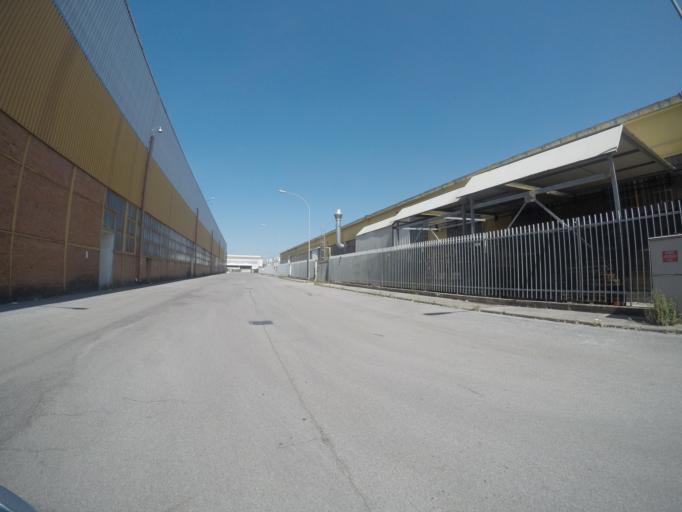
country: IT
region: Tuscany
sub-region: Provincia di Massa-Carrara
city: Massa
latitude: 44.0254
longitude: 10.1044
